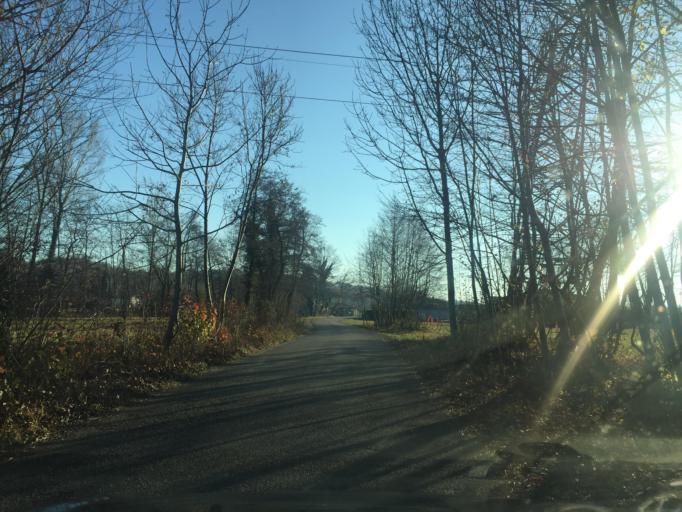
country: IT
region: Friuli Venezia Giulia
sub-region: Provincia di Udine
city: Buia
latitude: 46.2397
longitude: 13.1131
